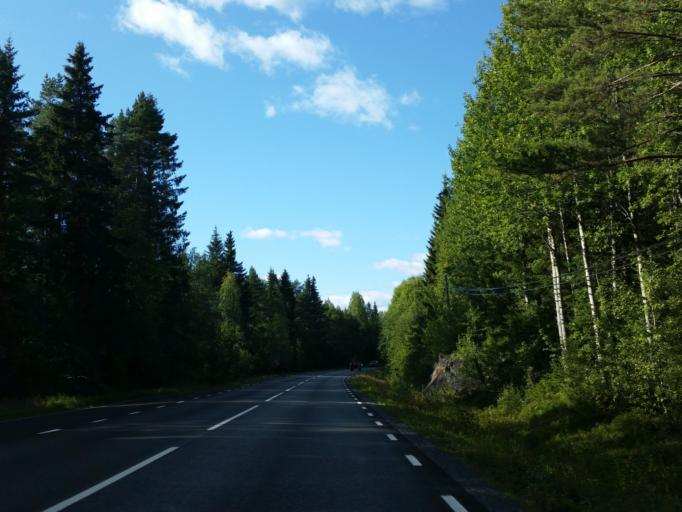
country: SE
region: Vaesterbotten
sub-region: Robertsfors Kommun
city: Robertsfors
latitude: 64.1618
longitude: 20.9370
